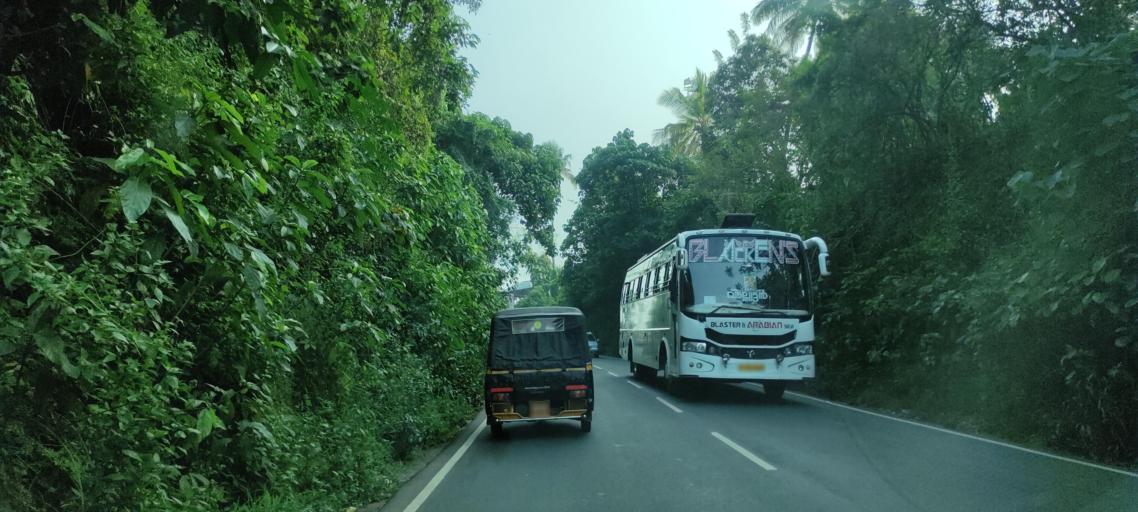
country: IN
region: Kerala
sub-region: Kottayam
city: Vaikam
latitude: 9.7607
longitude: 76.4933
